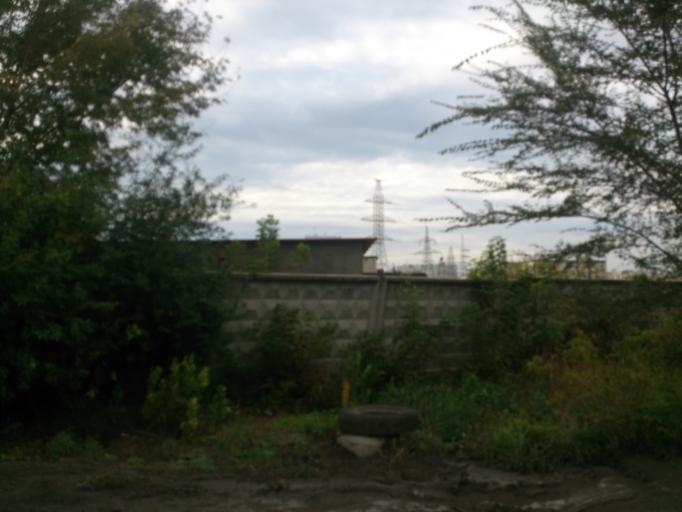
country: RU
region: Ulyanovsk
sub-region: Ulyanovskiy Rayon
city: Ulyanovsk
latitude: 54.2813
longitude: 48.3055
